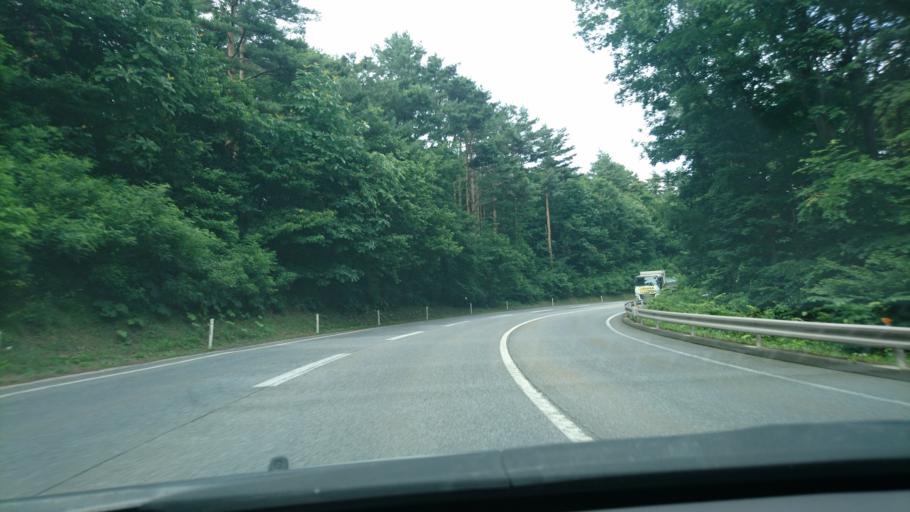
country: JP
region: Aomori
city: Hachinohe
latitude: 40.2342
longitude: 141.7789
